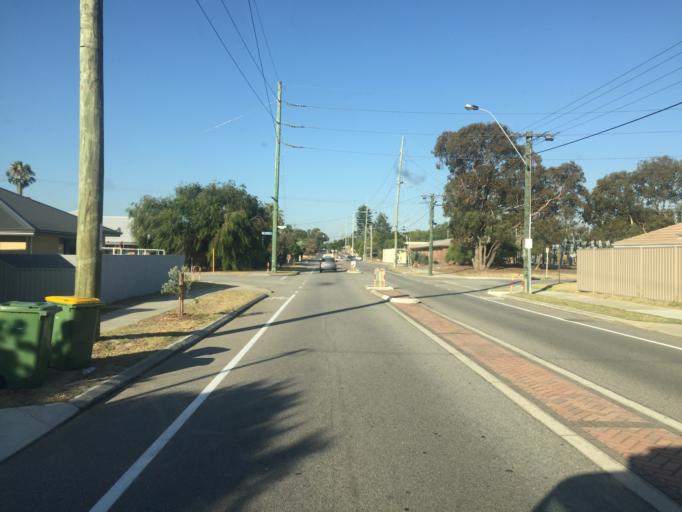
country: AU
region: Western Australia
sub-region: Belmont
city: Belmont
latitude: -31.9559
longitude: 115.9343
